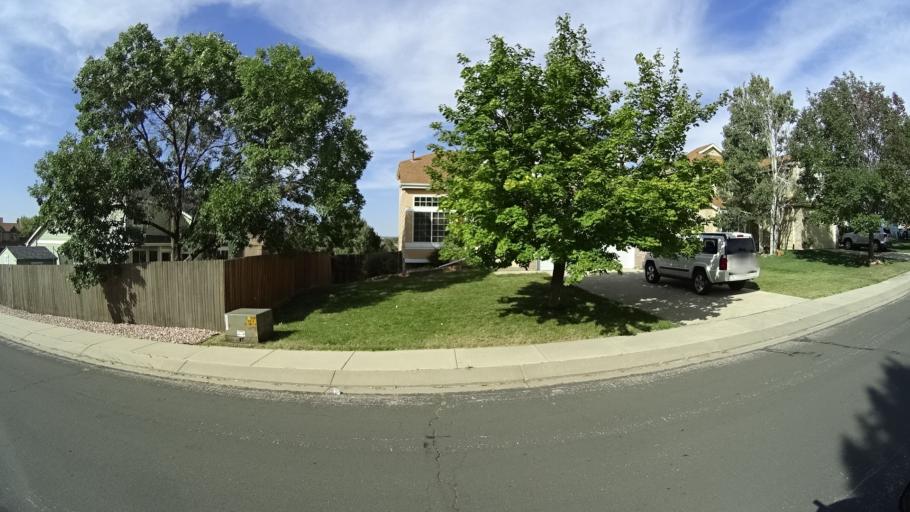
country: US
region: Colorado
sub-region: El Paso County
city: Cimarron Hills
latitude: 38.9041
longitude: -104.6923
